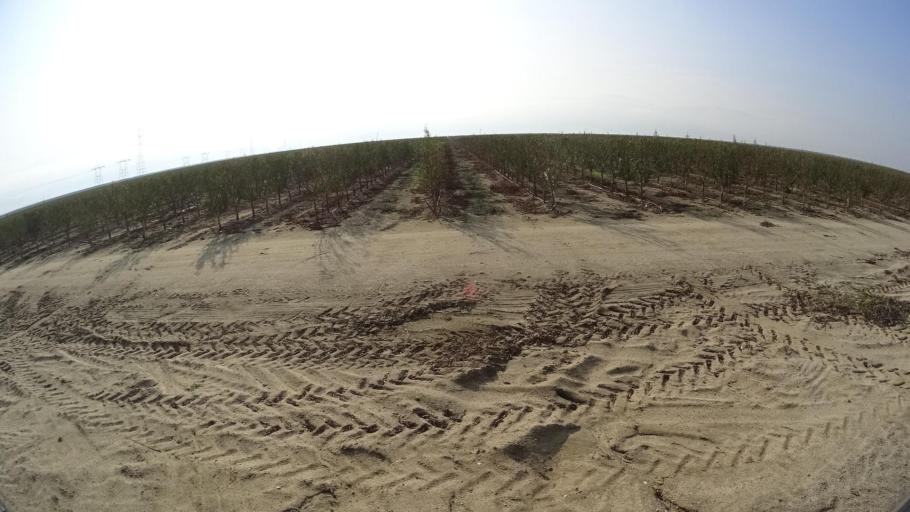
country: US
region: California
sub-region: Kern County
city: Lebec
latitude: 34.9930
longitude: -118.8615
